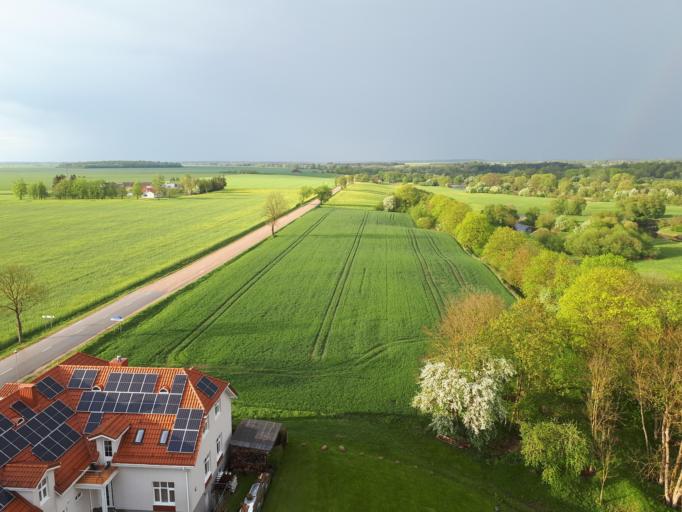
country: LT
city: Ramygala
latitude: 55.5517
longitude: 24.1056
